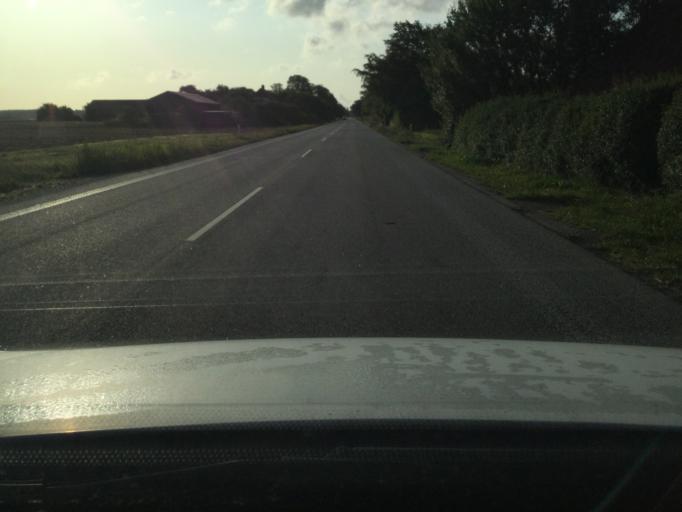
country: DK
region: Zealand
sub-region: Lolland Kommune
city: Rodby
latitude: 54.7636
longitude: 11.3186
